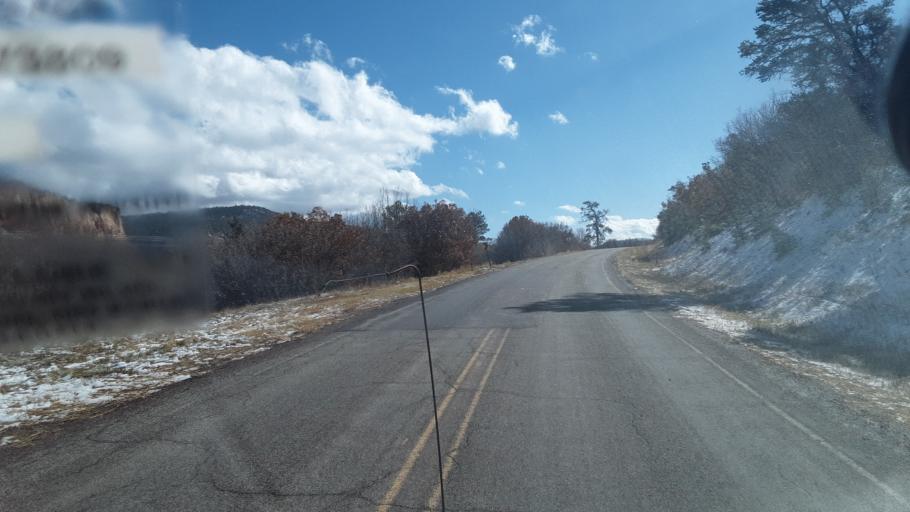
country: US
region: New Mexico
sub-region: Rio Arriba County
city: Santa Teresa
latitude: 36.2300
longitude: -106.8034
